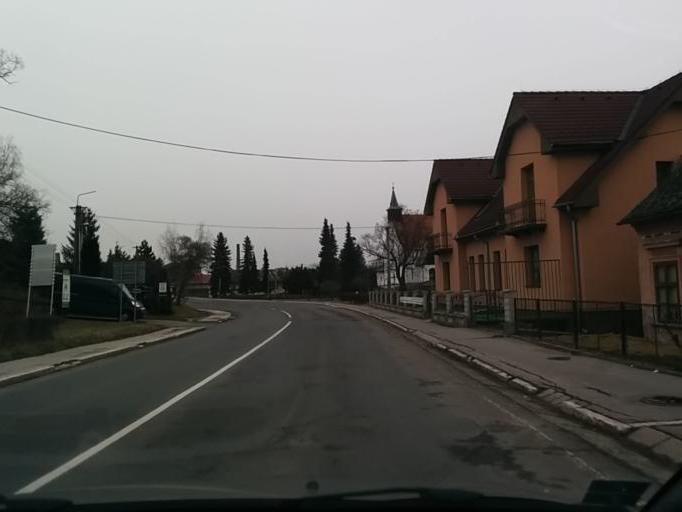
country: SK
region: Banskobystricky
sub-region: Okres Banska Bystrica
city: Zvolen
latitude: 48.6166
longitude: 19.1363
